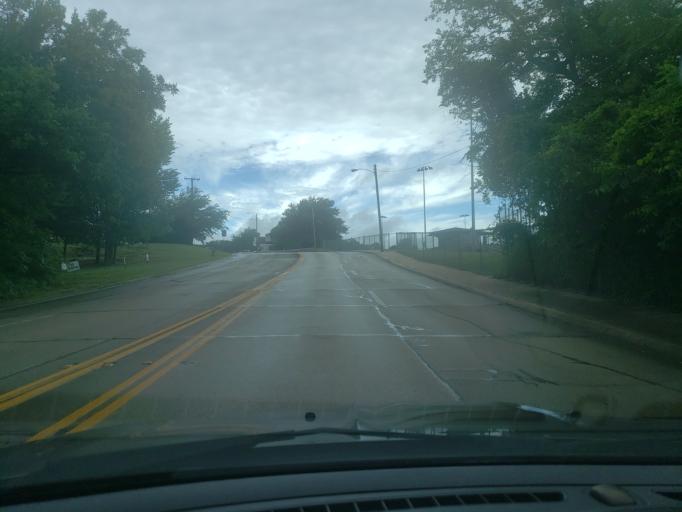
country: US
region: Texas
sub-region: Dallas County
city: Grand Prairie
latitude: 32.7499
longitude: -97.0037
